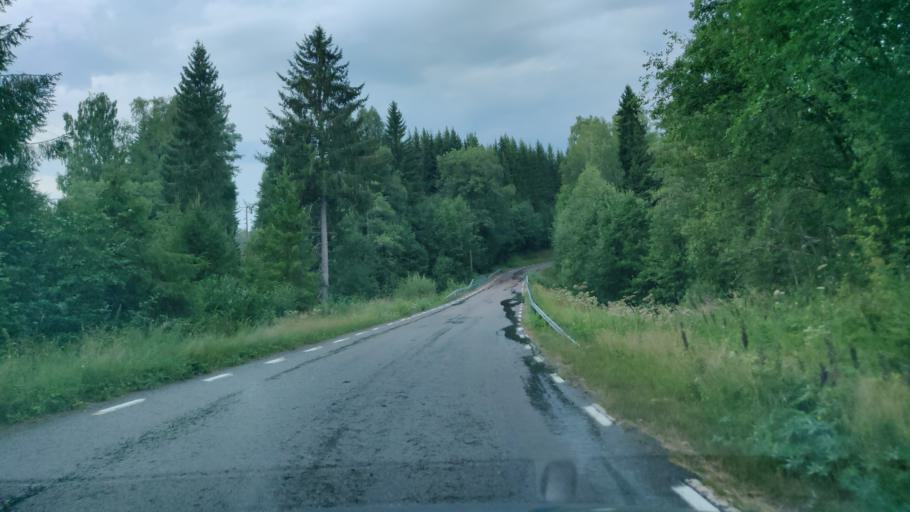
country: SE
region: Vaermland
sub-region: Munkfors Kommun
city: Munkfors
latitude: 59.8751
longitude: 13.5238
